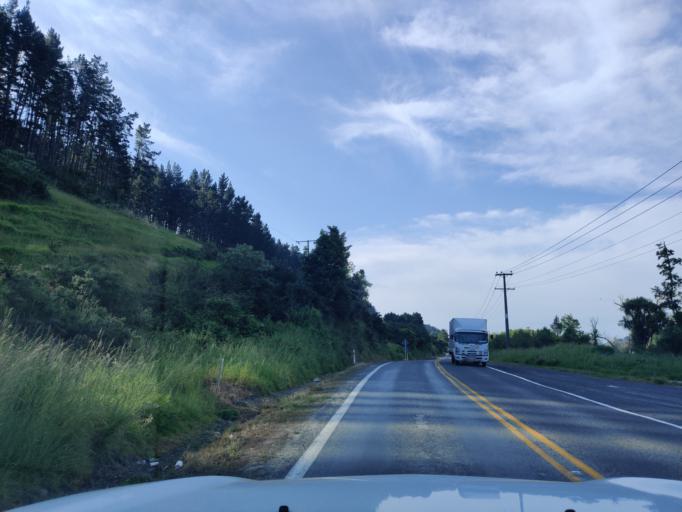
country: NZ
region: Waikato
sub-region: Waikato District
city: Ngaruawahia
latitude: -37.5888
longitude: 175.1549
